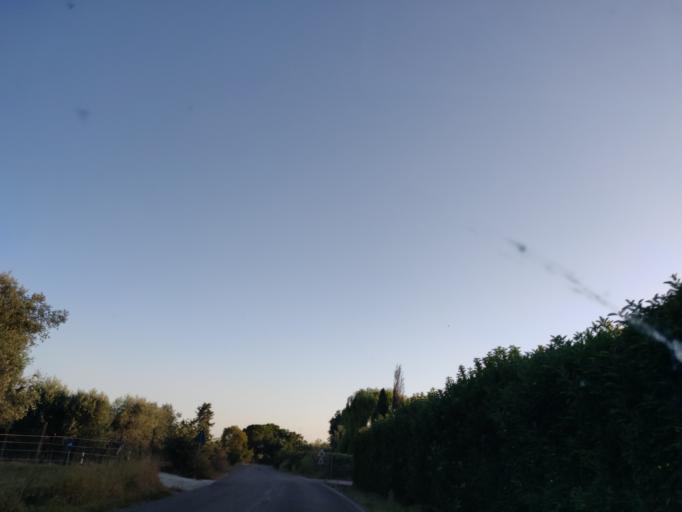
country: IT
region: Latium
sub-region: Provincia di Viterbo
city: Canino
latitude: 42.4173
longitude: 11.7043
